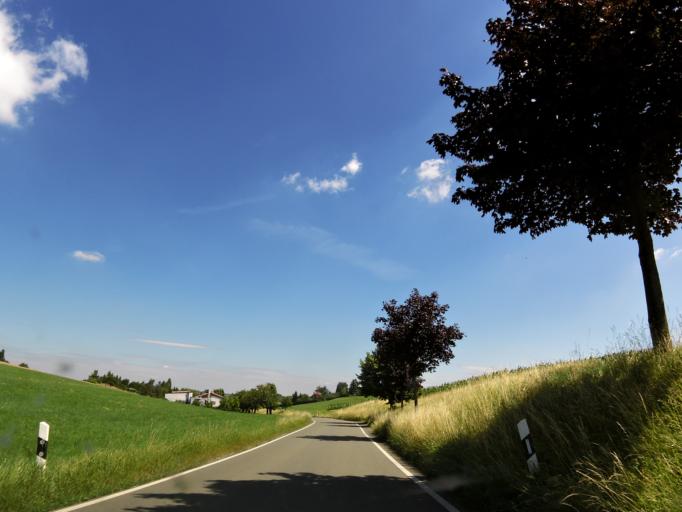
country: DE
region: Thuringia
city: Kraftsdorf
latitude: 50.8921
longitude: 11.9460
